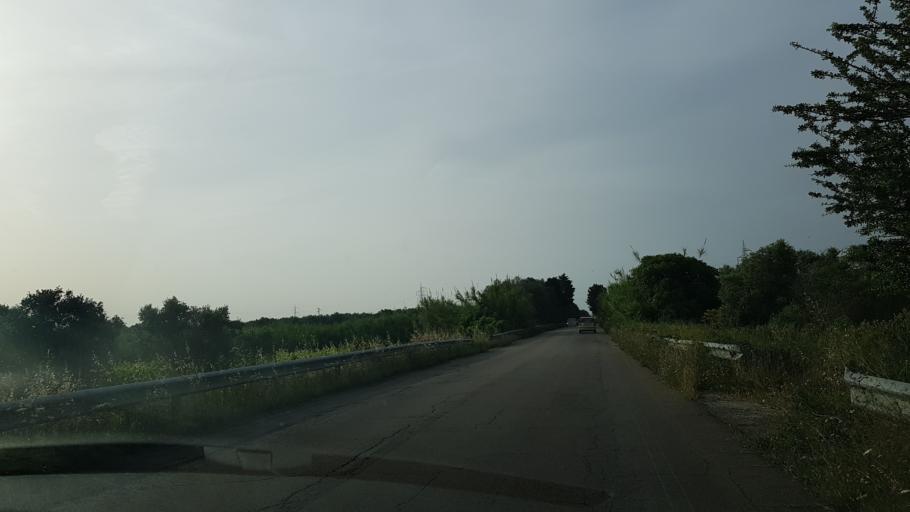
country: IT
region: Apulia
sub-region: Provincia di Brindisi
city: Tuturano
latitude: 40.5343
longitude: 17.9814
